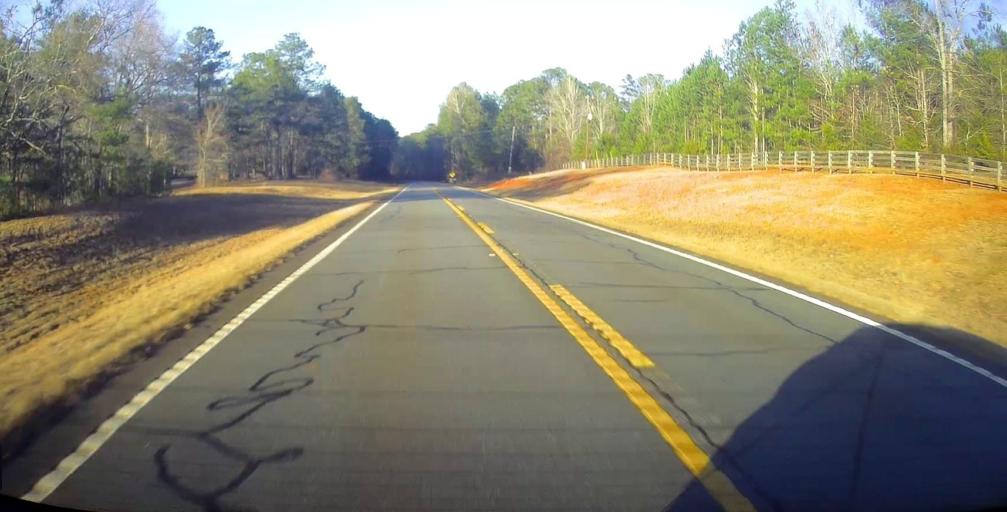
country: US
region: Georgia
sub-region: Talbot County
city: Talbotton
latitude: 32.7934
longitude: -84.5061
